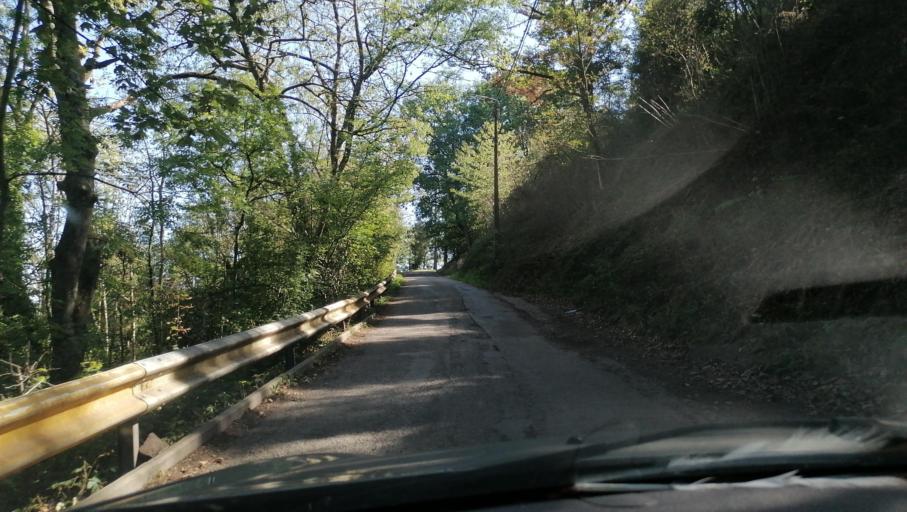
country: BE
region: Wallonia
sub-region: Province de Namur
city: Profondeville
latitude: 50.3566
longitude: 4.8648
